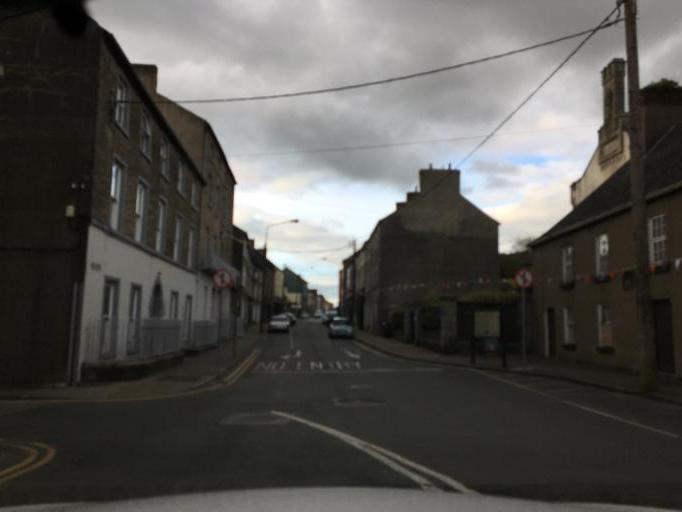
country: IE
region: Leinster
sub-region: Loch Garman
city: New Ross
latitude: 52.3929
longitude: -6.9455
